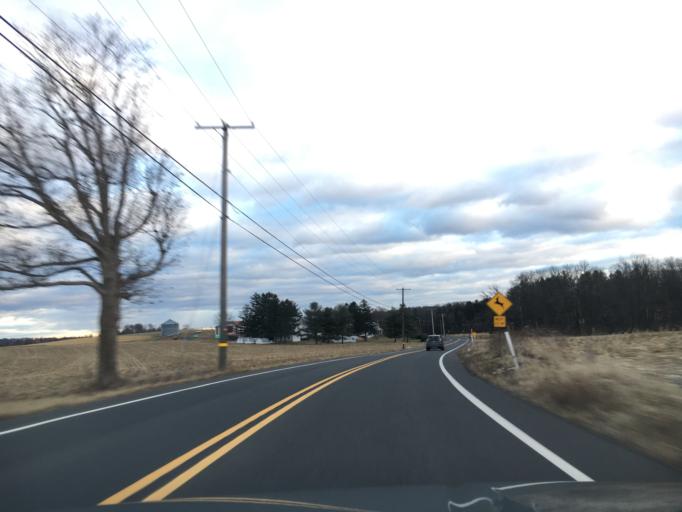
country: US
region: Pennsylvania
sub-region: Lehigh County
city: Schnecksville
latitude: 40.6847
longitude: -75.6655
